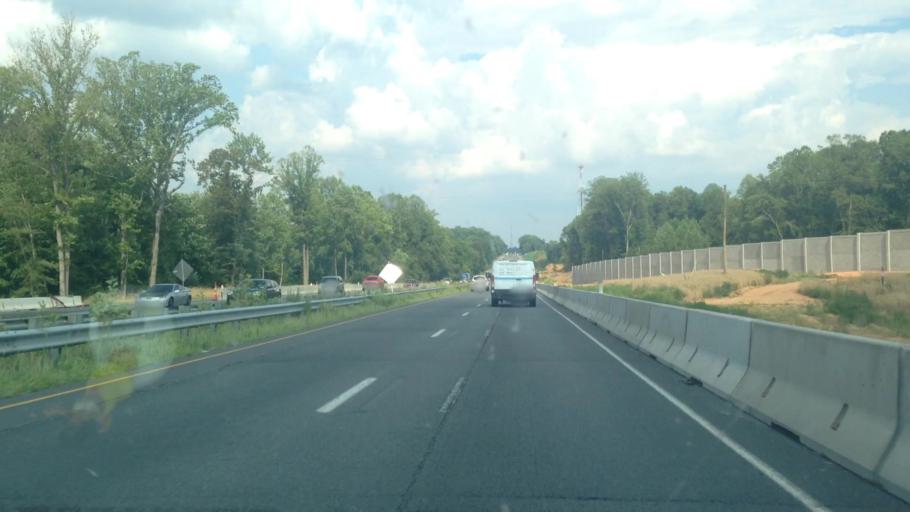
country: US
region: North Carolina
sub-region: Forsyth County
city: Kernersville
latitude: 36.1124
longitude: -80.1241
